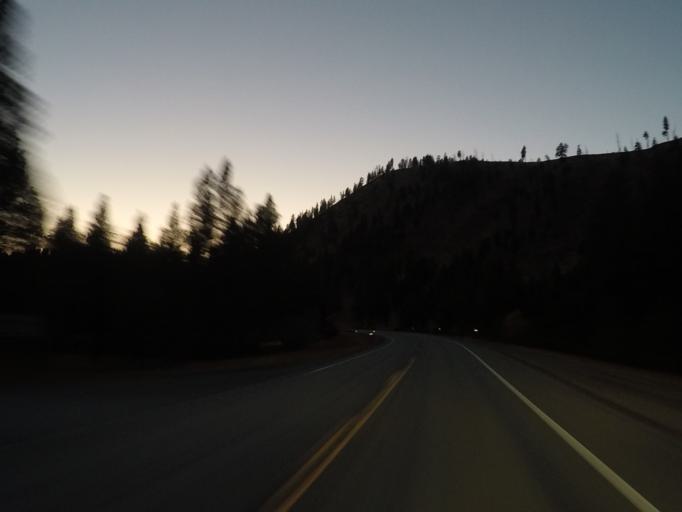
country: US
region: Montana
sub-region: Missoula County
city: Seeley Lake
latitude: 47.0247
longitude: -113.3049
